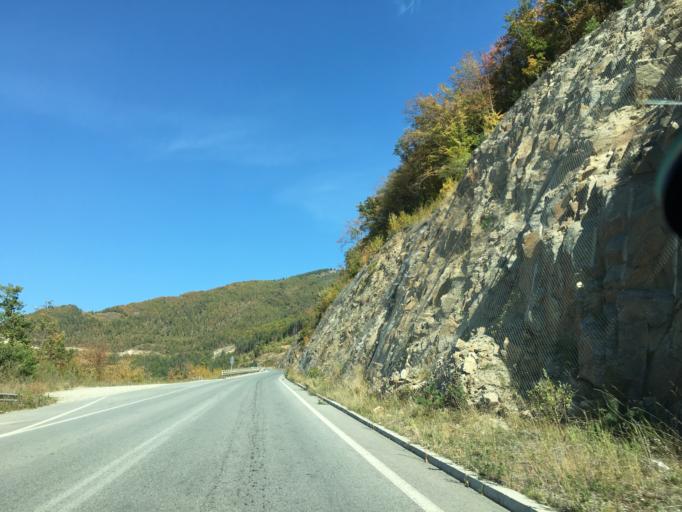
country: BG
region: Smolyan
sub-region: Obshtina Devin
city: Devin
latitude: 41.7627
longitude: 24.4405
